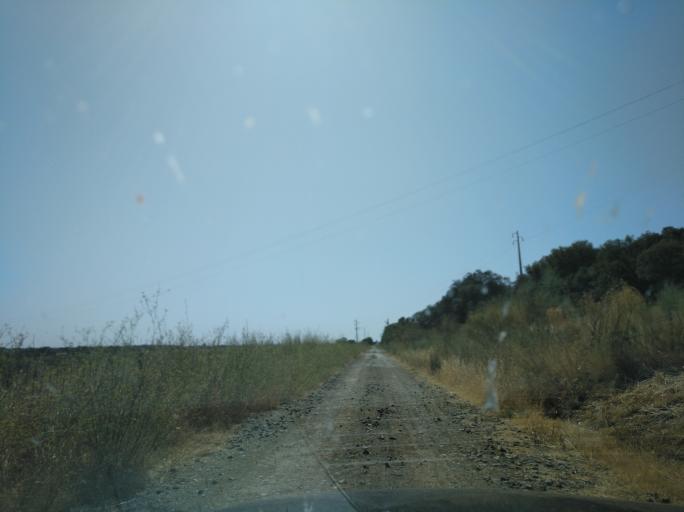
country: PT
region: Portalegre
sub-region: Campo Maior
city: Campo Maior
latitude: 39.0597
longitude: -7.0077
